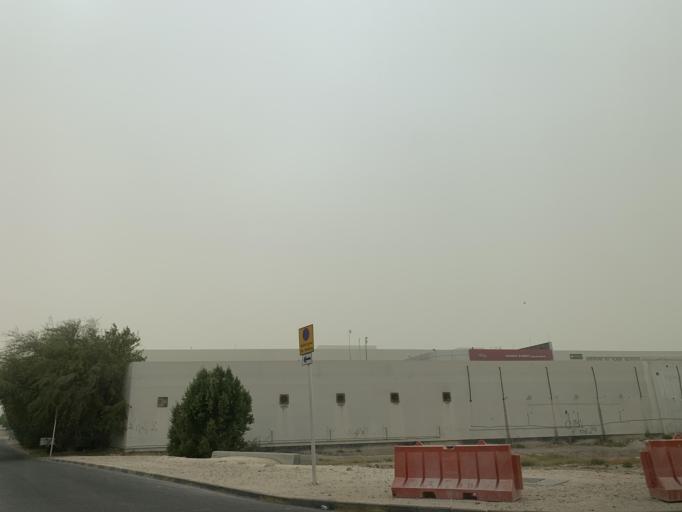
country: BH
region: Central Governorate
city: Madinat Hamad
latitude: 26.1360
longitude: 50.5213
